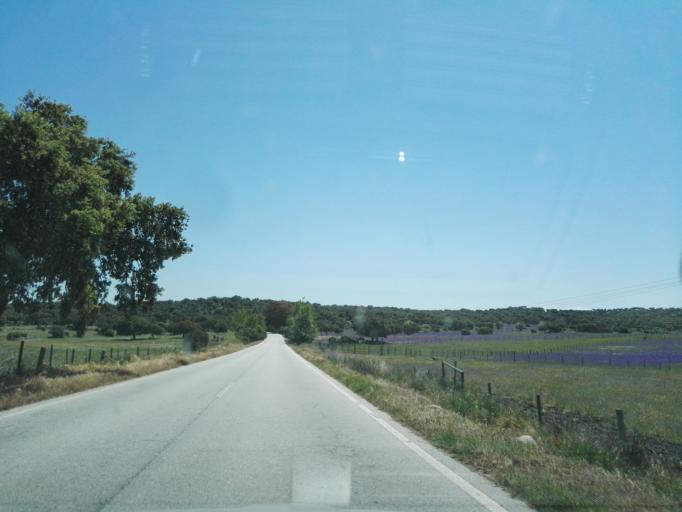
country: PT
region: Portalegre
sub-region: Arronches
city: Arronches
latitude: 39.0031
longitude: -7.2253
